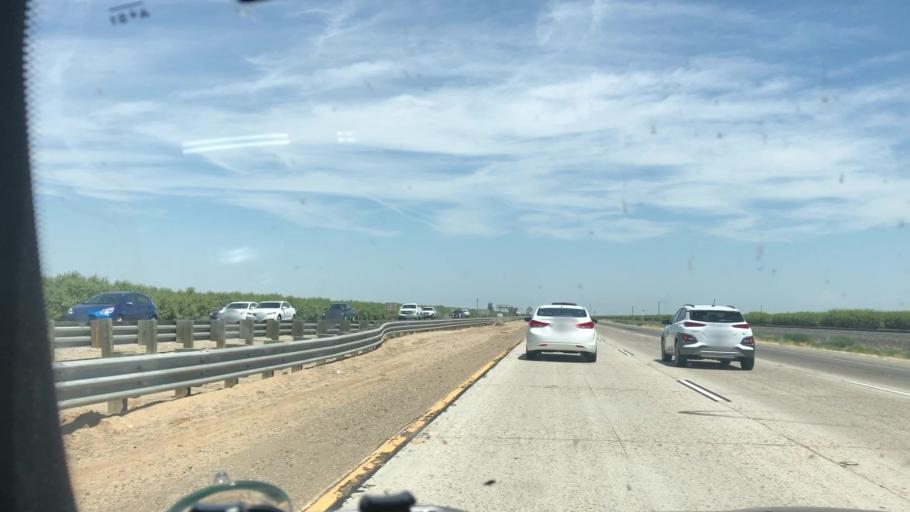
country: US
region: California
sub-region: Kern County
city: McFarland
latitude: 35.6191
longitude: -119.2133
